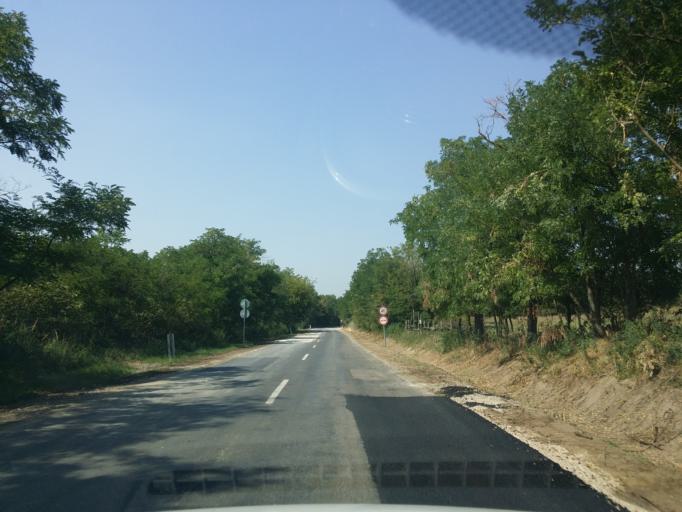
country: HU
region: Tolna
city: Pincehely
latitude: 46.6210
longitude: 18.4175
